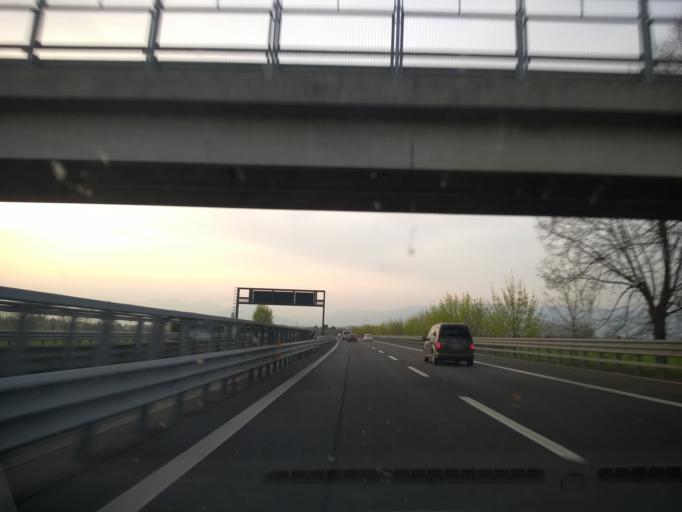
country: IT
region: Veneto
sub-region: Provincia di Vicenza
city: Vigardolo
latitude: 45.6259
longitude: 11.5922
